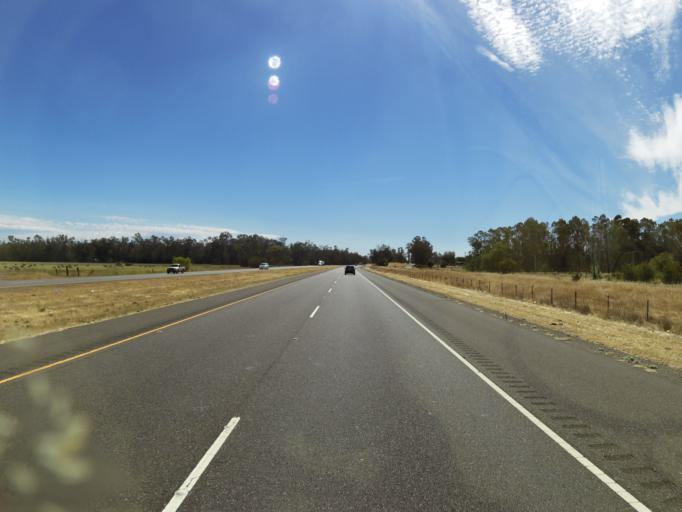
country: US
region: California
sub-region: Solano County
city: Hartley
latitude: 38.4296
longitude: -121.9427
